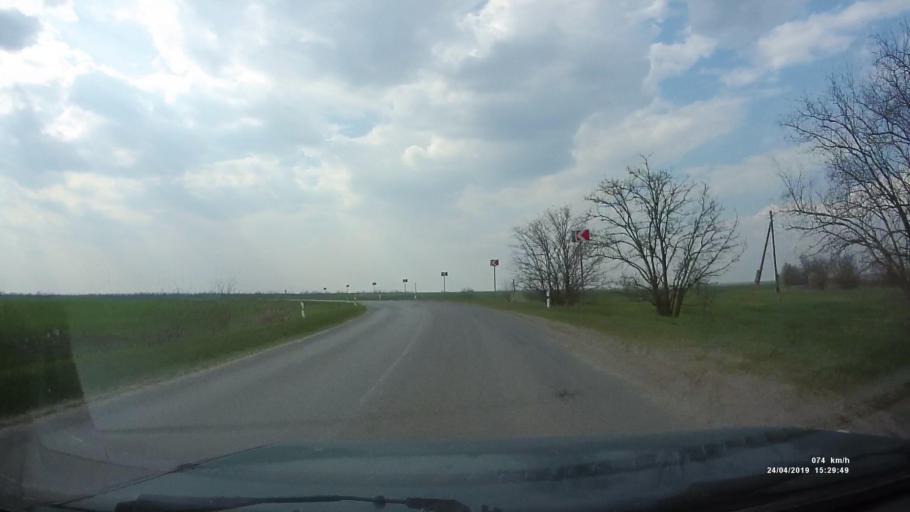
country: RU
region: Rostov
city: Remontnoye
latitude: 46.5990
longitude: 43.0174
